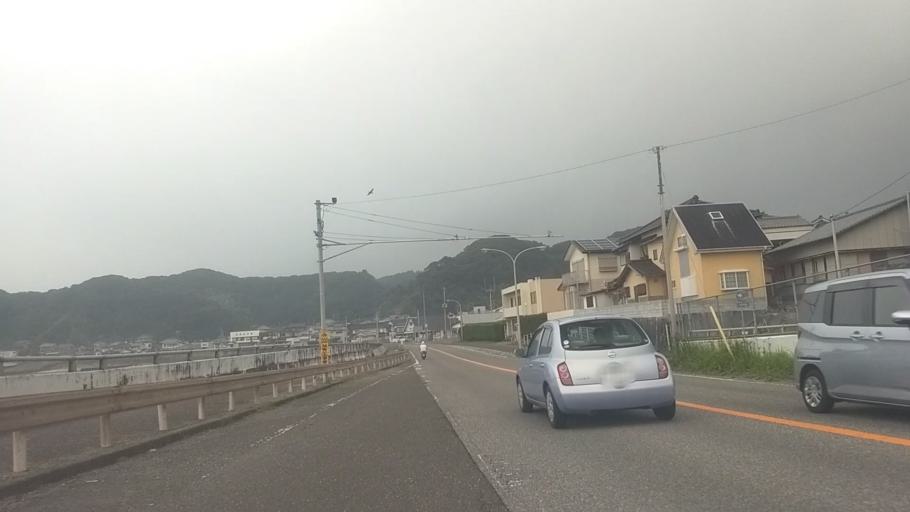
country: JP
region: Chiba
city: Katsuura
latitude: 35.1513
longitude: 140.3015
